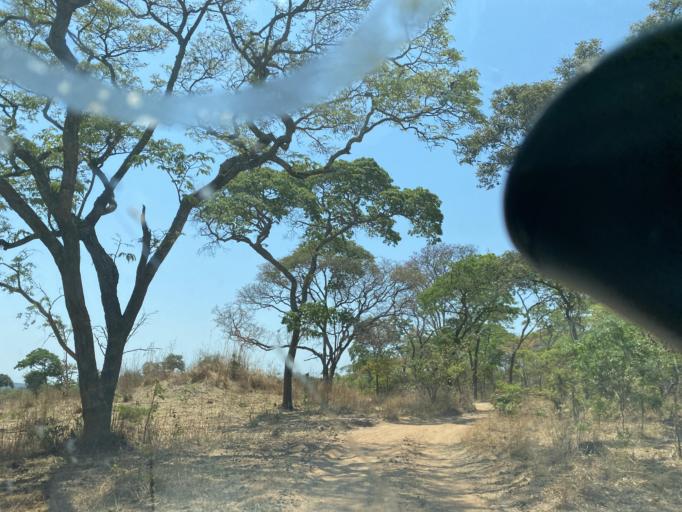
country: ZM
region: Lusaka
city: Chongwe
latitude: -15.4263
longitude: 29.1818
